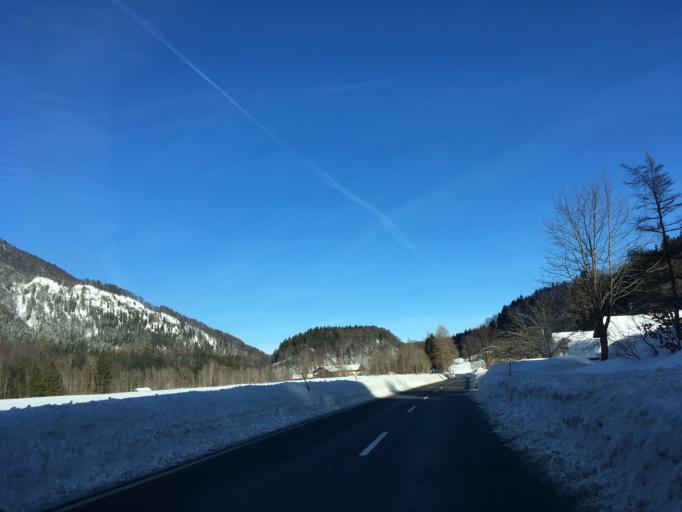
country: DE
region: Bavaria
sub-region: Upper Bavaria
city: Aschau im Chiemgau
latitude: 47.7420
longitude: 12.3075
